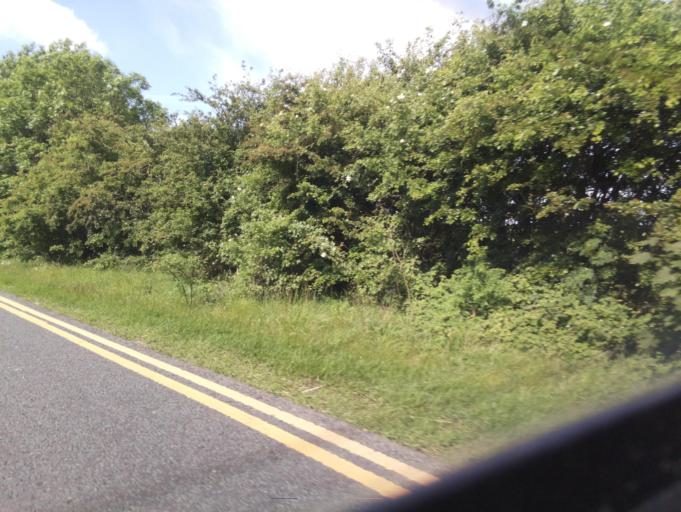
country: GB
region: England
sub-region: Lincolnshire
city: Burton
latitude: 53.3114
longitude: -0.5356
